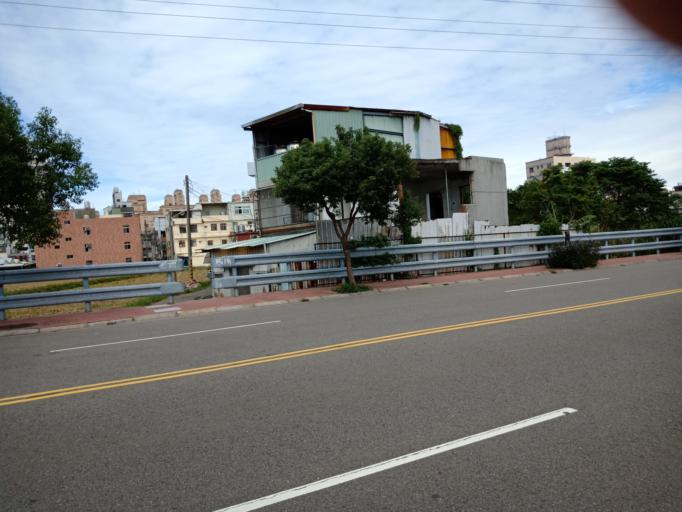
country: TW
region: Taiwan
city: Taoyuan City
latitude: 24.9495
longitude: 121.2583
